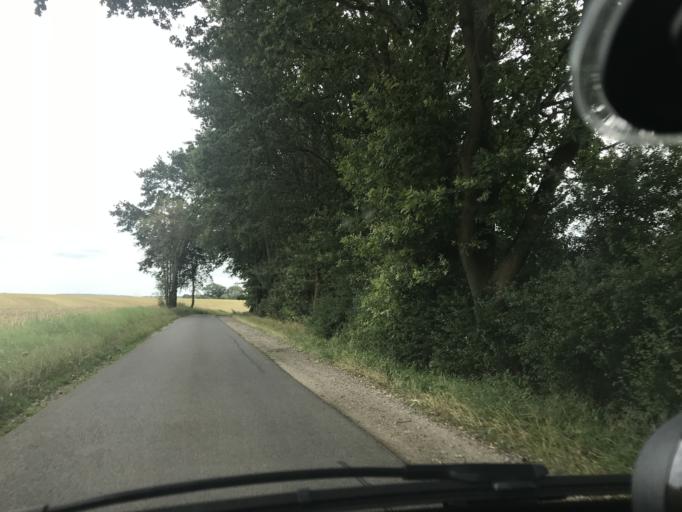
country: DE
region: Lower Saxony
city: Moisburg
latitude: 53.4013
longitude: 9.7132
